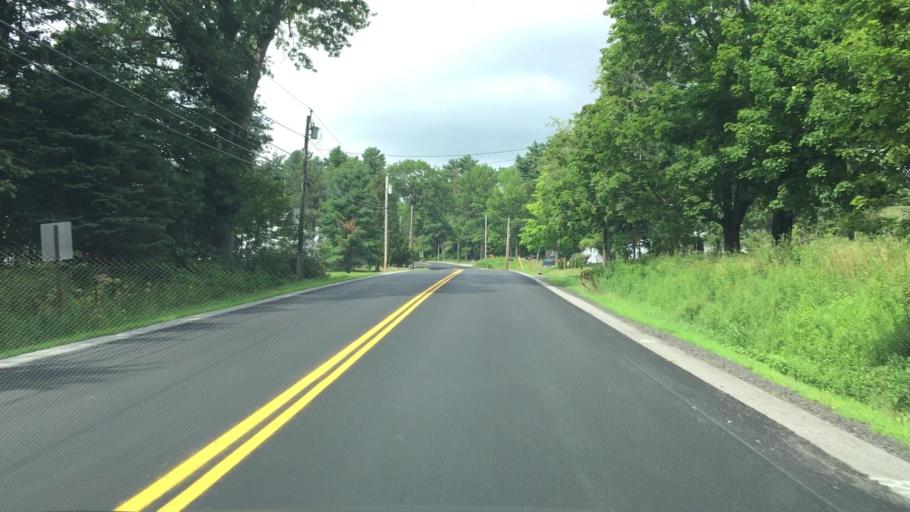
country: US
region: Maine
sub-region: Hancock County
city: Bucksport
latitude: 44.6025
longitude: -68.8164
